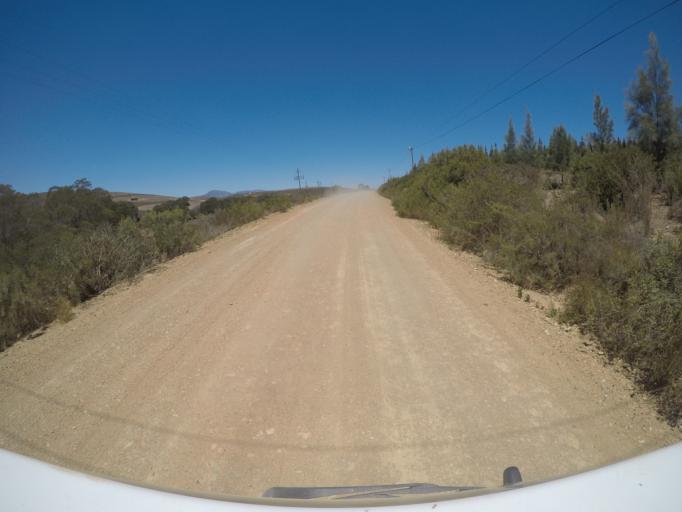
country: ZA
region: Western Cape
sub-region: Overberg District Municipality
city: Caledon
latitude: -34.1710
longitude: 19.2294
